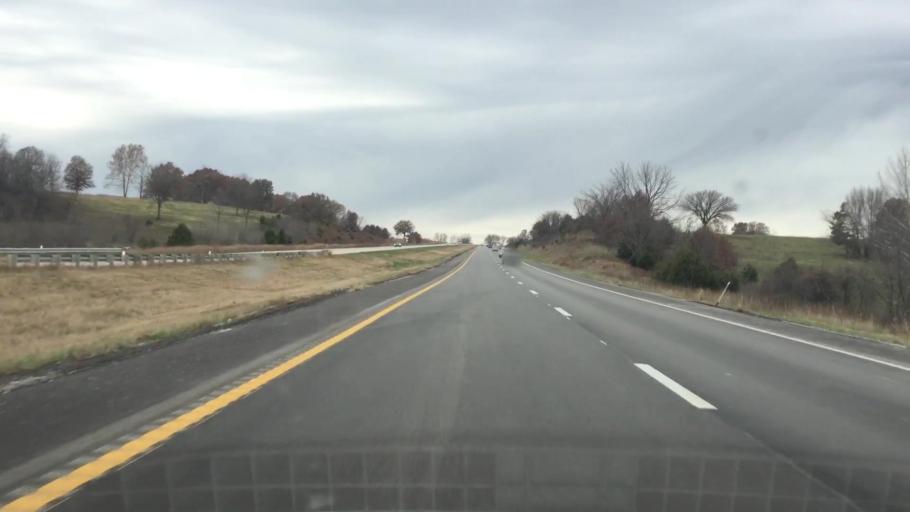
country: US
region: Missouri
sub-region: Saint Clair County
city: Osceola
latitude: 38.0184
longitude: -93.6656
